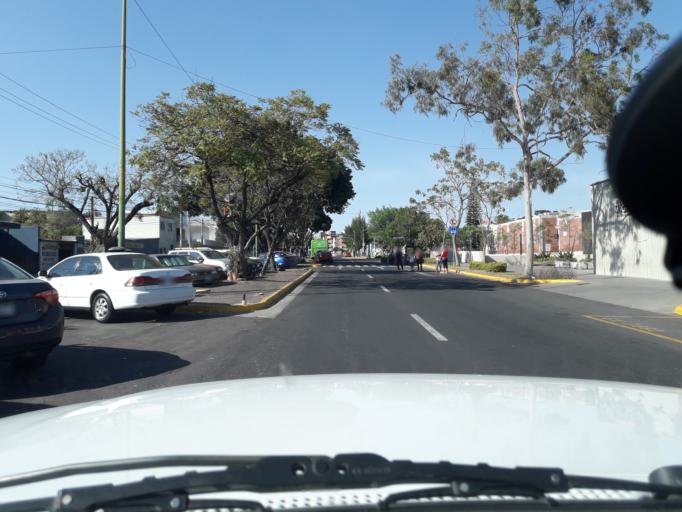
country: MX
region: Jalisco
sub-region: Zapopan
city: Zapopan
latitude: 20.6921
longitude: -103.3517
